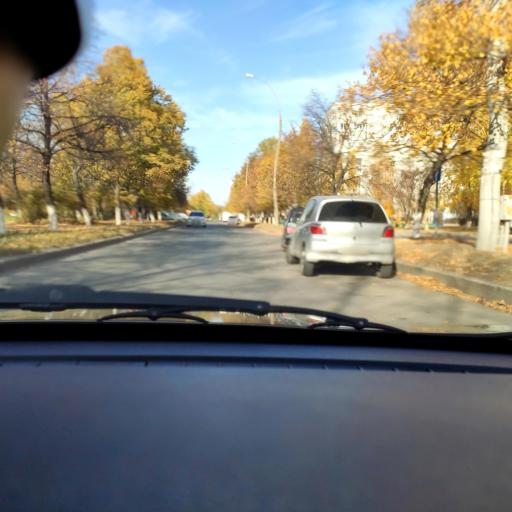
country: RU
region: Samara
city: Tol'yatti
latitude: 53.5308
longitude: 49.3134
